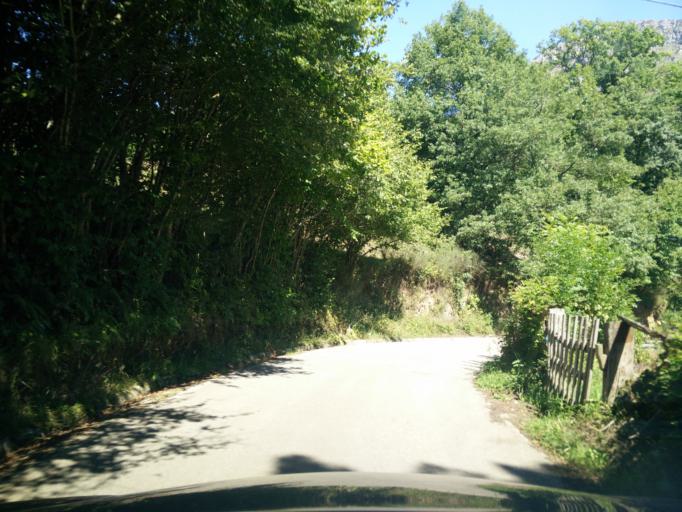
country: ES
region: Asturias
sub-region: Province of Asturias
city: Amieva
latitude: 43.1981
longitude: -5.1272
